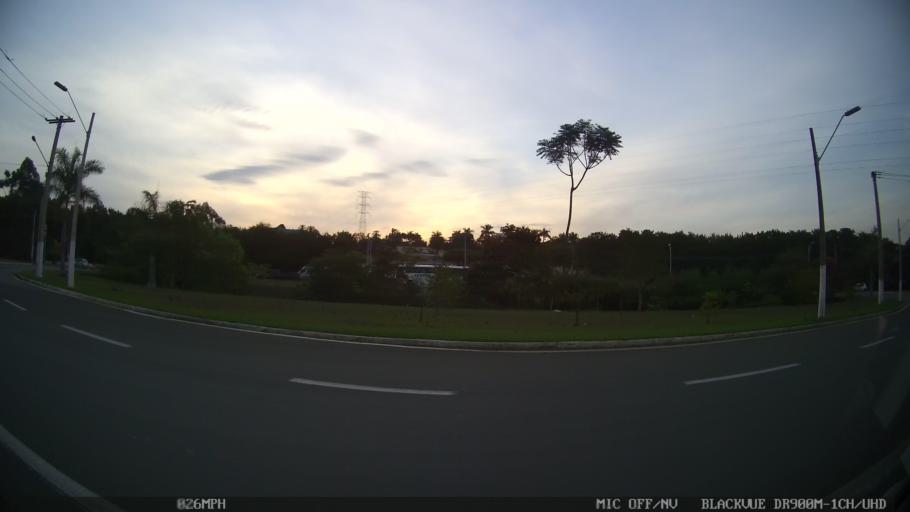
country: BR
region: Sao Paulo
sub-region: Limeira
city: Limeira
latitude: -22.5442
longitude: -47.4128
